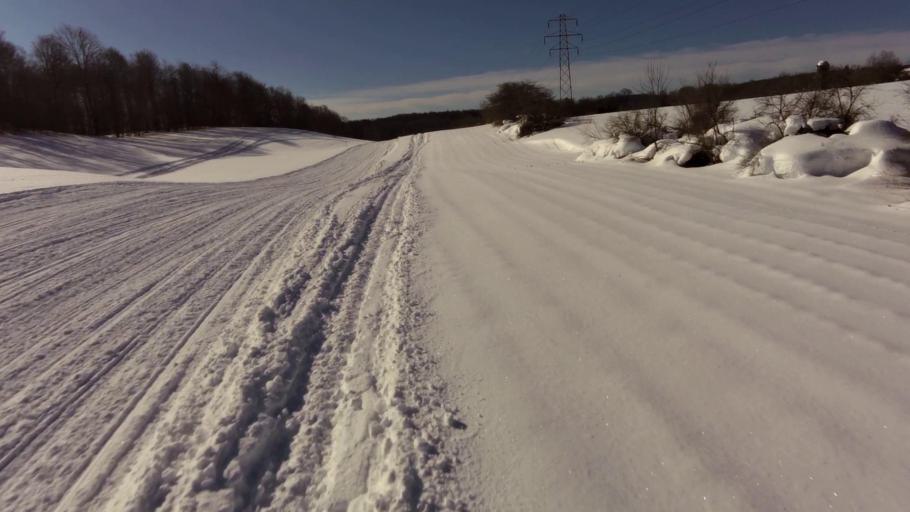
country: US
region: New York
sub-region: Cattaraugus County
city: Franklinville
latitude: 42.3953
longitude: -78.4925
